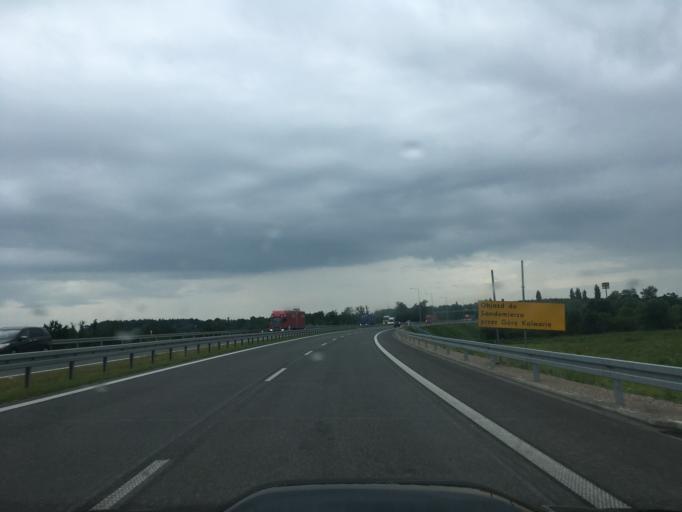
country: PL
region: Masovian Voivodeship
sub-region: Powiat piaseczynski
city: Gora Kalwaria
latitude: 51.9738
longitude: 21.2235
